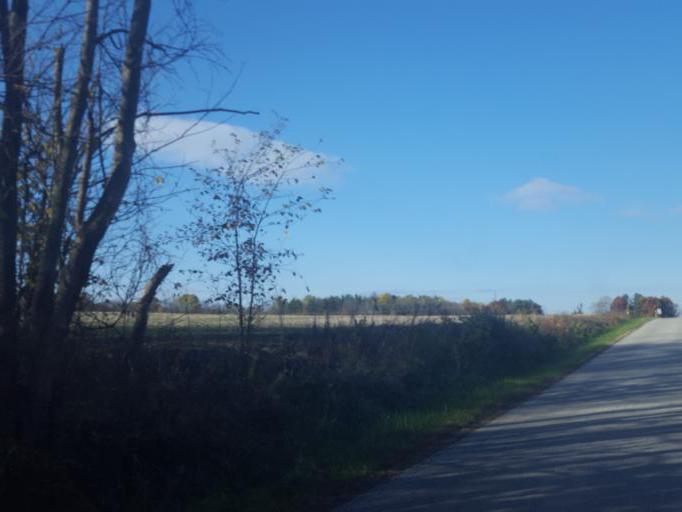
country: US
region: Ohio
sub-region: Crawford County
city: Galion
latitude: 40.6391
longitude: -82.7439
